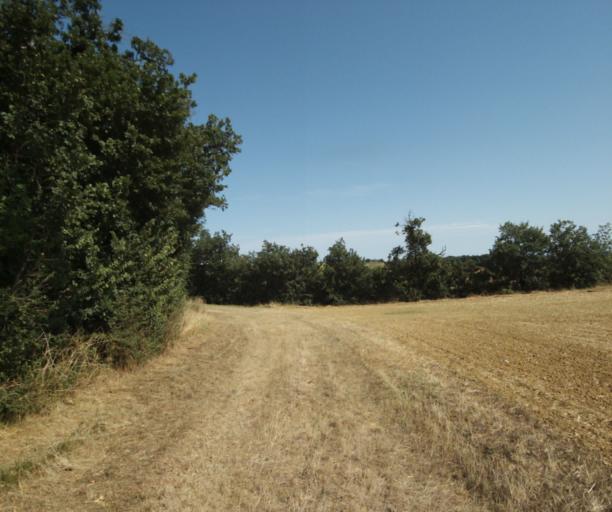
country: FR
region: Midi-Pyrenees
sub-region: Departement de la Haute-Garonne
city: Saint-Felix-Lauragais
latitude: 43.4393
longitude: 1.8459
